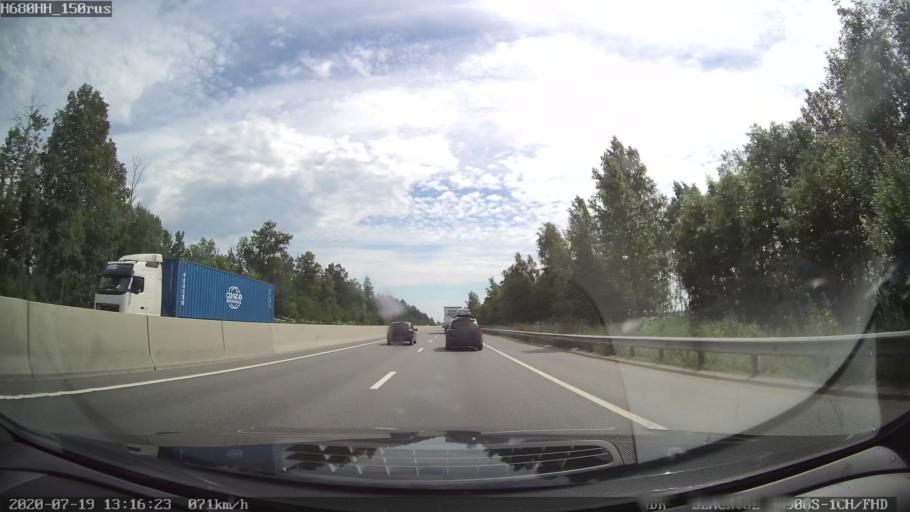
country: RU
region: St.-Petersburg
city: Kolpino
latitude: 59.7175
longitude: 30.5540
